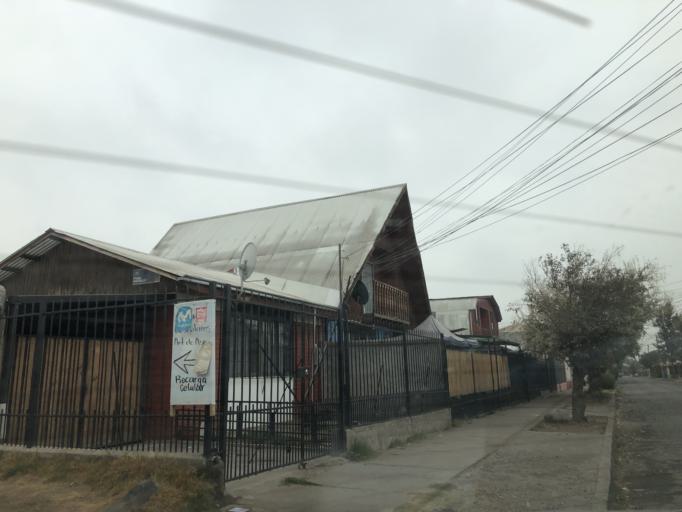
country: CL
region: Santiago Metropolitan
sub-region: Provincia de Cordillera
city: Puente Alto
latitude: -33.5844
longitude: -70.5927
